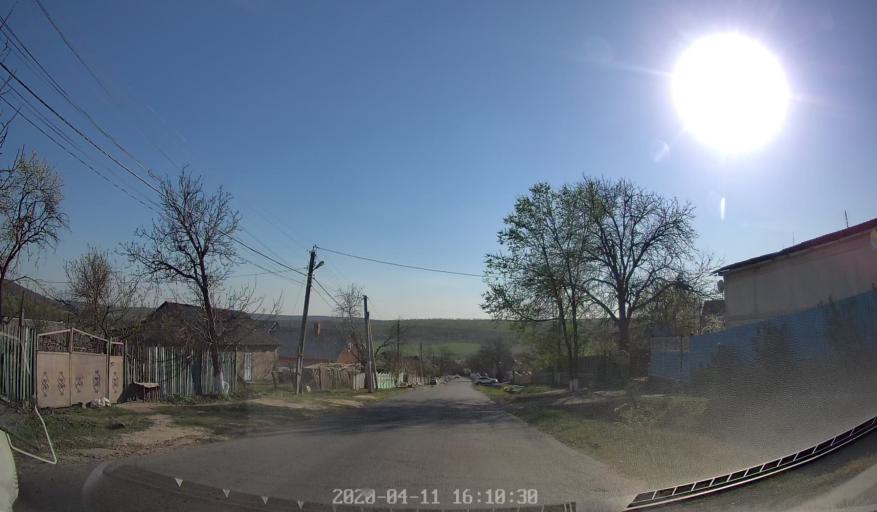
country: MD
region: Chisinau
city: Vadul lui Voda
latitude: 47.0673
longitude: 29.1328
